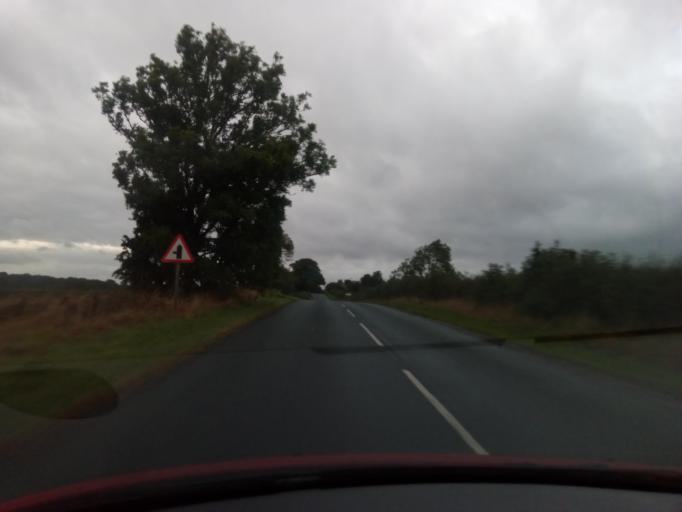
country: GB
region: England
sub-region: Darlington
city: High Coniscliffe
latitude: 54.4952
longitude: -1.6706
